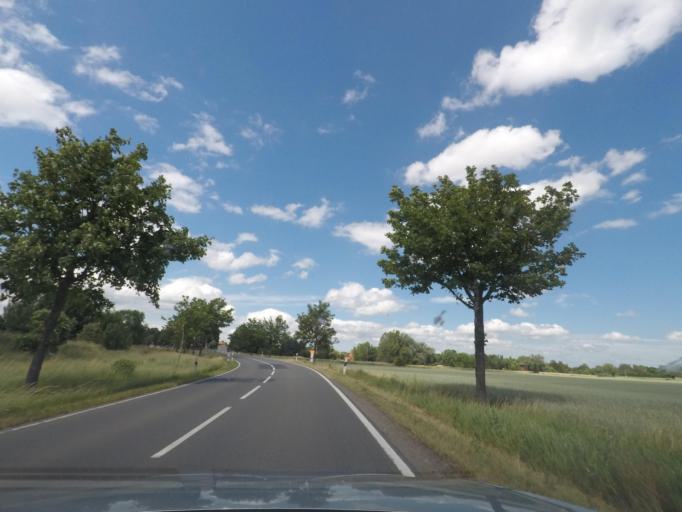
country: DE
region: Saxony-Anhalt
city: Gross Quenstedt
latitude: 51.9216
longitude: 11.1088
